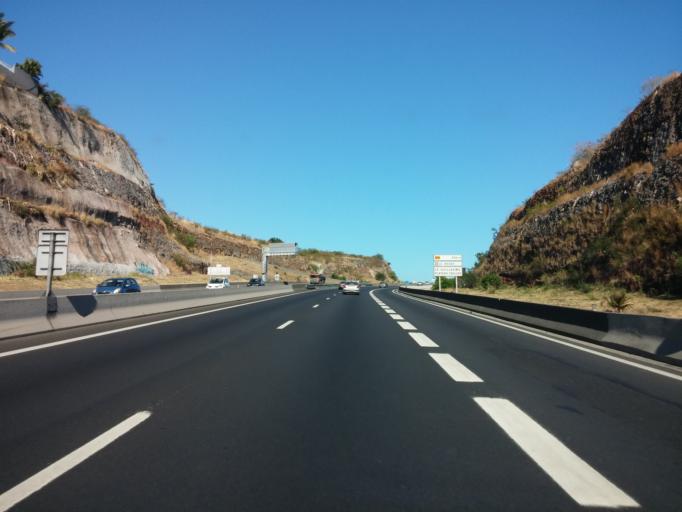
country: RE
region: Reunion
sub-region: Reunion
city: Saint-Paul
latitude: -21.0164
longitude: 55.2634
